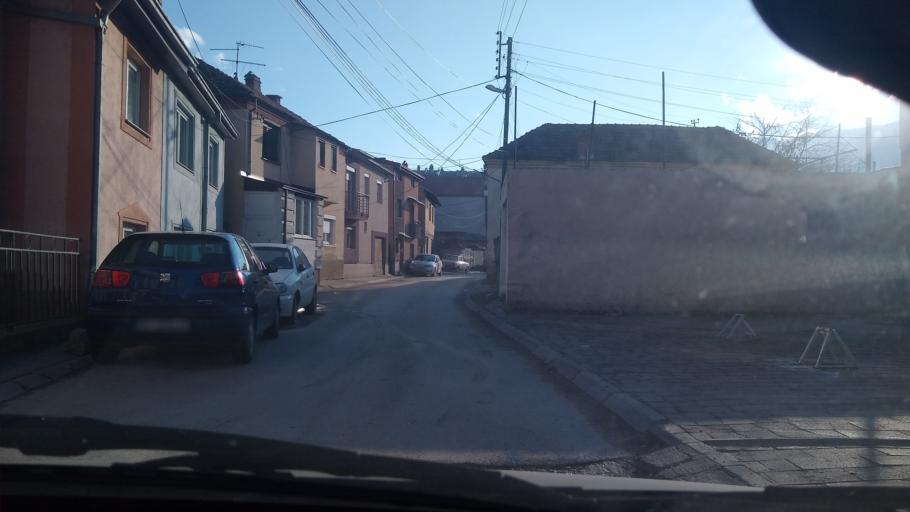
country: MK
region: Bitola
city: Bitola
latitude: 41.0254
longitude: 21.3243
